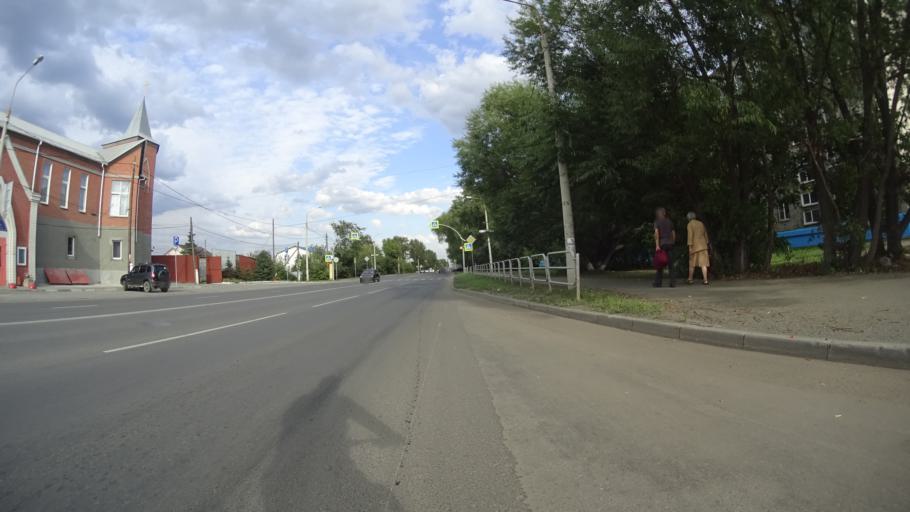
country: RU
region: Chelyabinsk
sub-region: Gorod Chelyabinsk
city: Chelyabinsk
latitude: 55.1985
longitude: 61.3430
